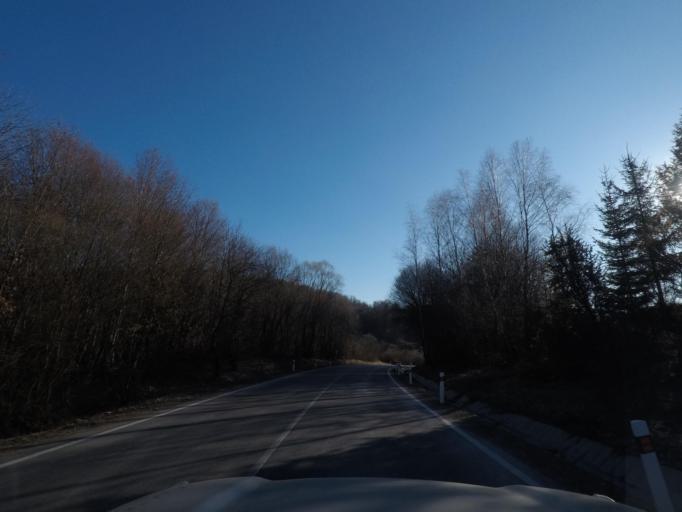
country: SK
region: Presovsky
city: Medzilaborce
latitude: 49.2846
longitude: 21.8480
